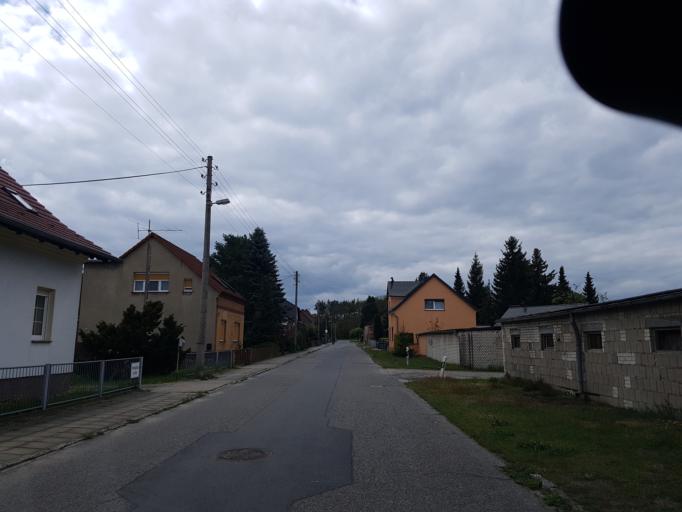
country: DE
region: Brandenburg
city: Altdobern
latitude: 51.6471
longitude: 14.0209
